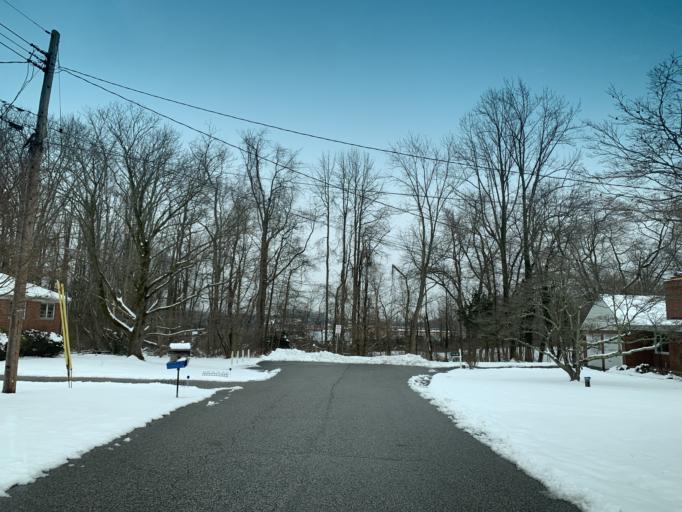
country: US
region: Maryland
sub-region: Harford County
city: Pleasant Hills
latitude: 39.4958
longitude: -76.3947
